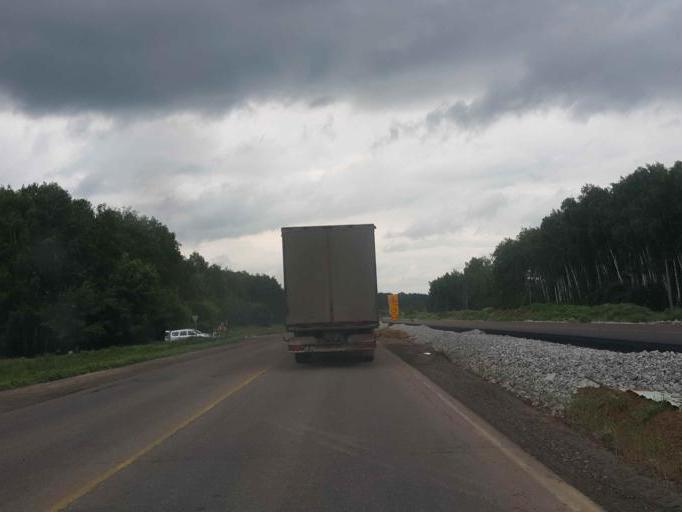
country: RU
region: Tambov
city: Selezni
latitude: 52.7769
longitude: 41.0403
